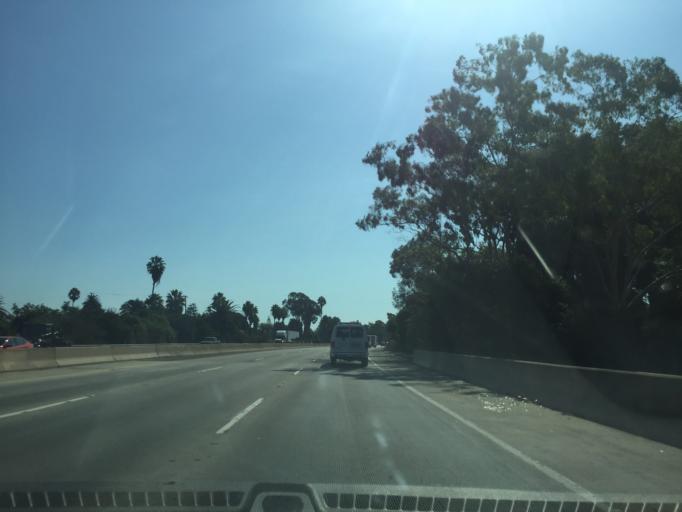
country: US
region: California
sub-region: Santa Barbara County
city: Santa Barbara
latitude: 34.4164
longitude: -119.7076
